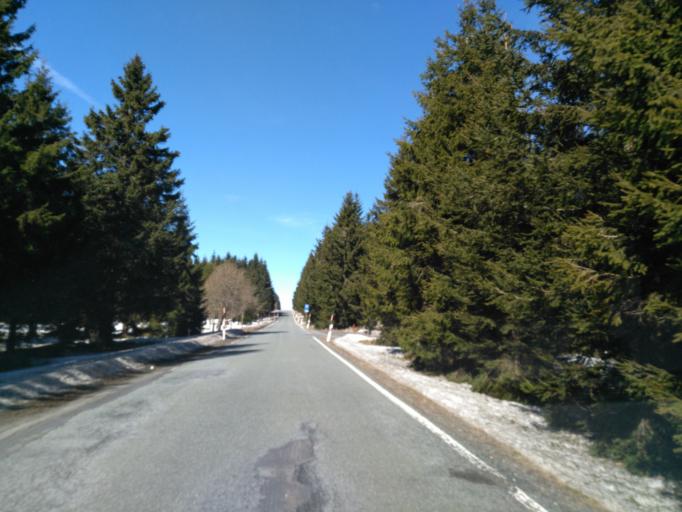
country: DE
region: Saxony
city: Kurort Oberwiesenthal
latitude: 50.4256
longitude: 12.9222
